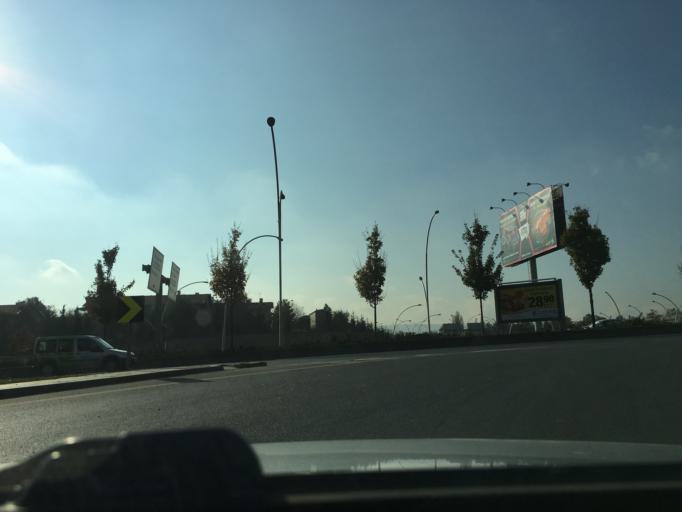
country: TR
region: Ankara
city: Ankara
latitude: 39.9091
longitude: 32.7869
